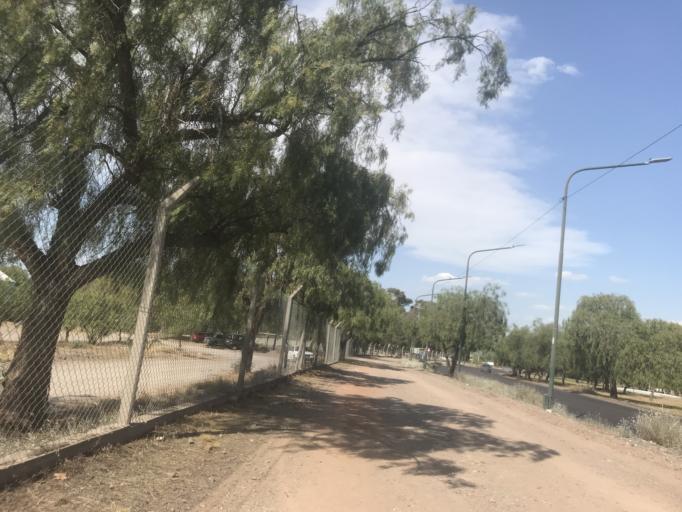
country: AR
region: Mendoza
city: Mendoza
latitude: -32.8821
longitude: -68.8846
